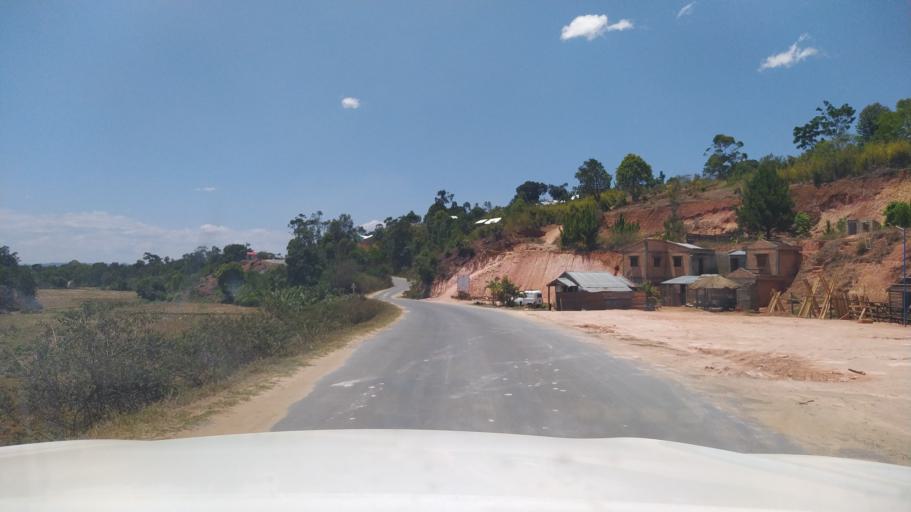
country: MG
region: Analamanga
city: Anjozorobe
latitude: -18.4467
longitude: 48.2631
